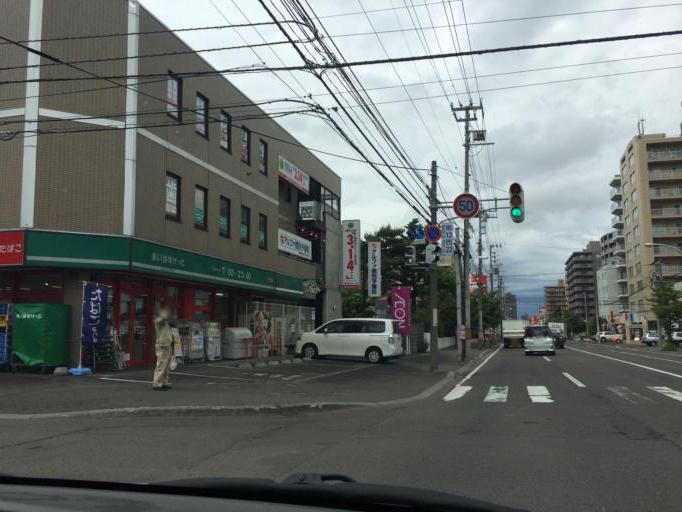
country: JP
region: Hokkaido
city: Sapporo
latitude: 43.0399
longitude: 141.3283
